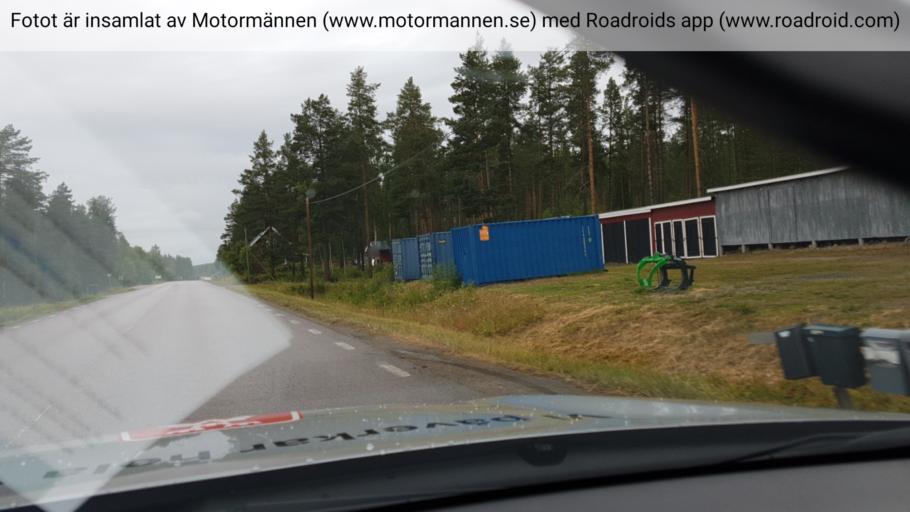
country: SE
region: Norrbotten
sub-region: Alvsbyns Kommun
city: AElvsbyn
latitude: 66.1094
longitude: 20.9323
